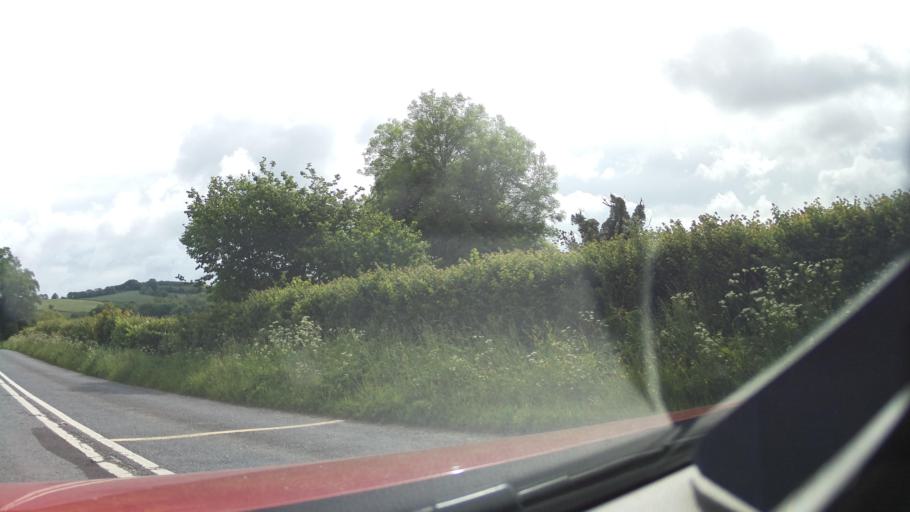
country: GB
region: England
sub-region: Devon
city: Chudleigh
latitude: 50.6133
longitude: -3.5893
